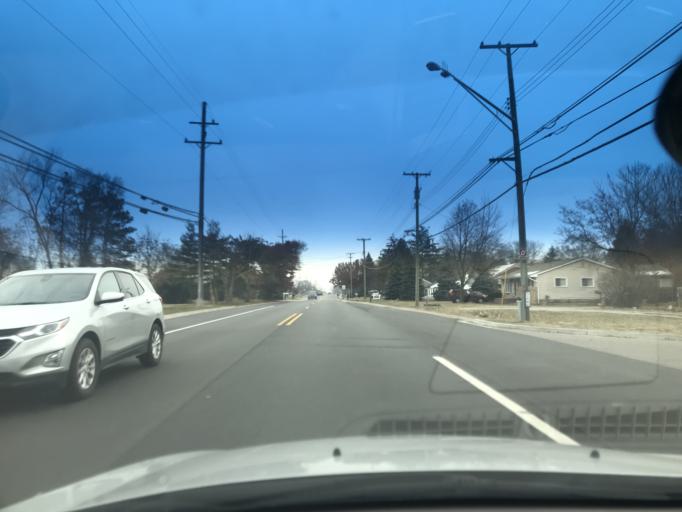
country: US
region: Michigan
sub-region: Macomb County
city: Shelby
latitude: 42.6550
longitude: -83.0394
